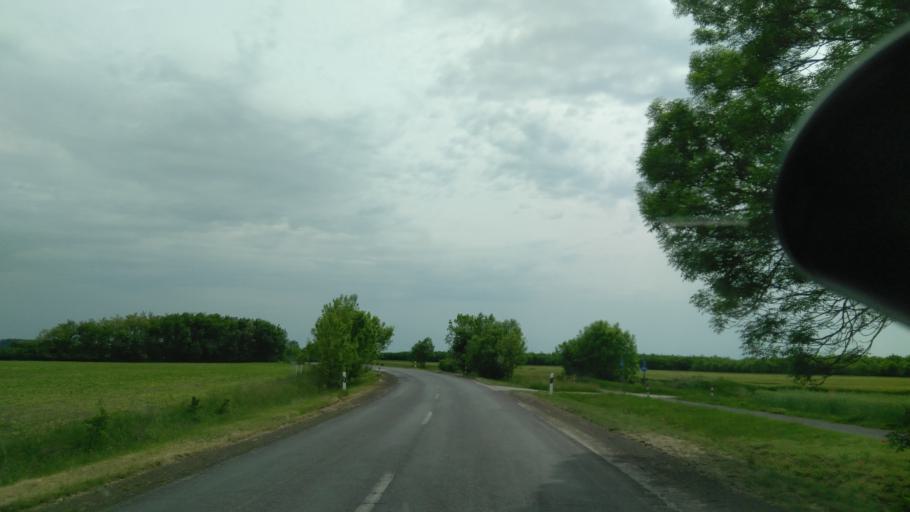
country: HU
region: Bekes
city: Sarkad
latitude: 46.7957
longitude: 21.3805
